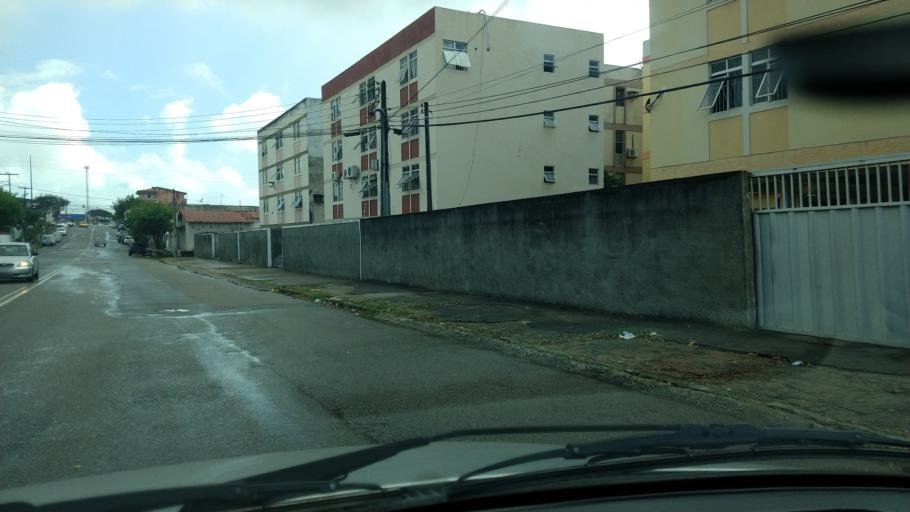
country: BR
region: Rio Grande do Norte
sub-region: Natal
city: Natal
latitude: -5.8105
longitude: -35.2183
